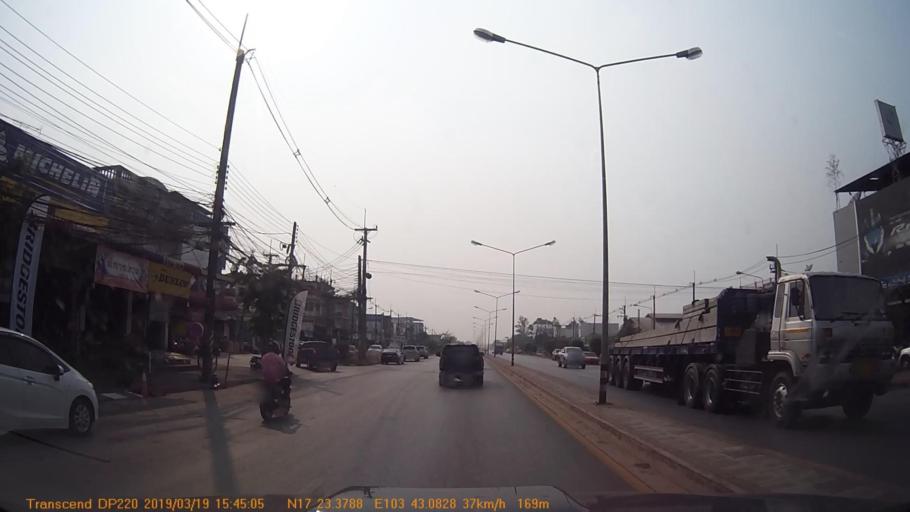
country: TH
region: Sakon Nakhon
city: Phang Khon
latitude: 17.3897
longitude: 103.7179
